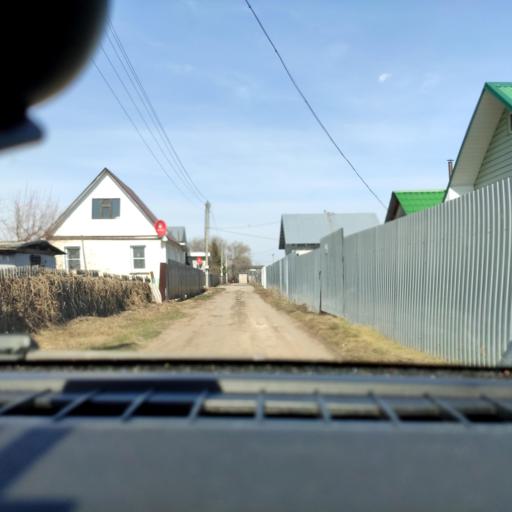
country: RU
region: Samara
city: Podstepki
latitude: 53.5189
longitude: 49.1083
